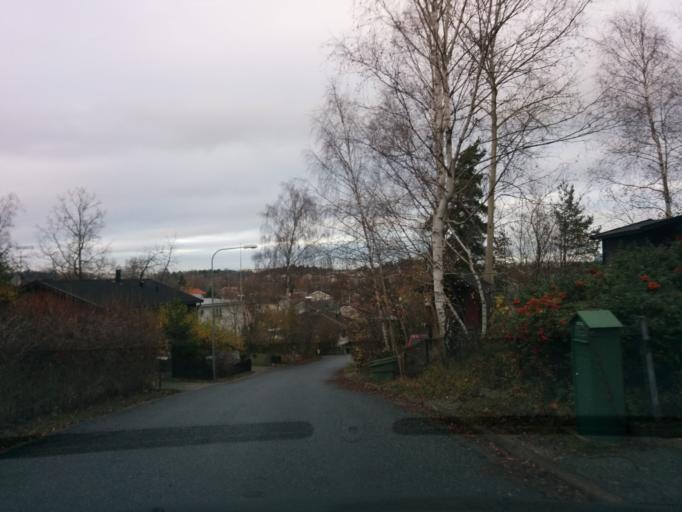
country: SE
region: Stockholm
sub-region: Stockholms Kommun
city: Kista
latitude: 59.3741
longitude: 17.9102
